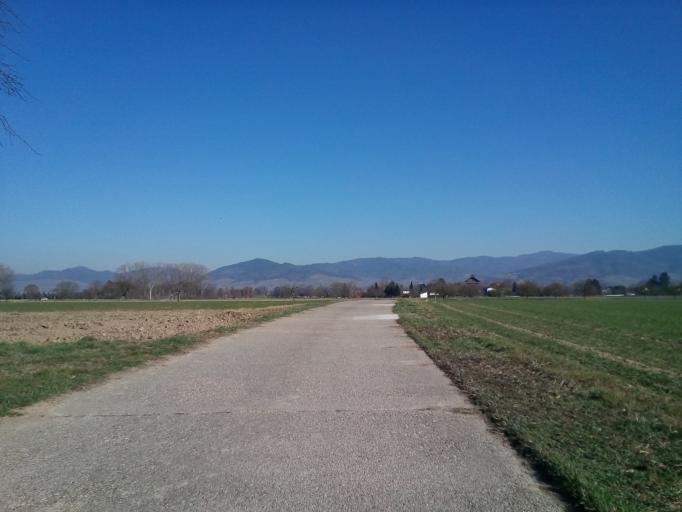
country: DE
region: Baden-Wuerttemberg
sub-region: Karlsruhe Region
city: Ottersweier
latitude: 48.7023
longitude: 8.1007
